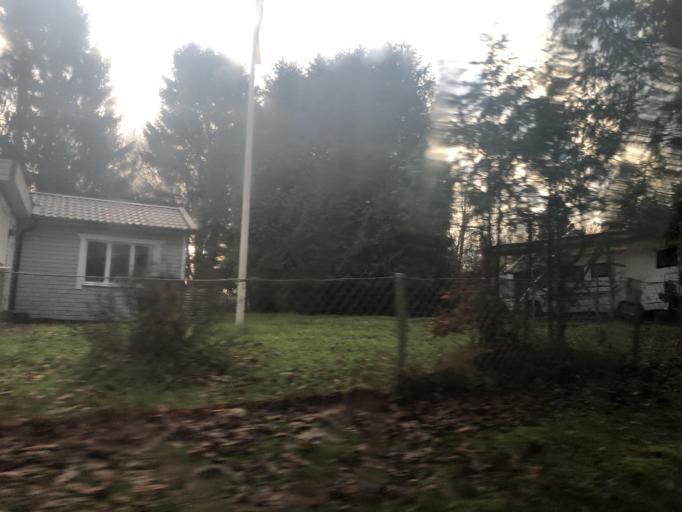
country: SE
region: Skane
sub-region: Sjobo Kommun
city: Blentarp
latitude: 55.6052
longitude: 13.5403
